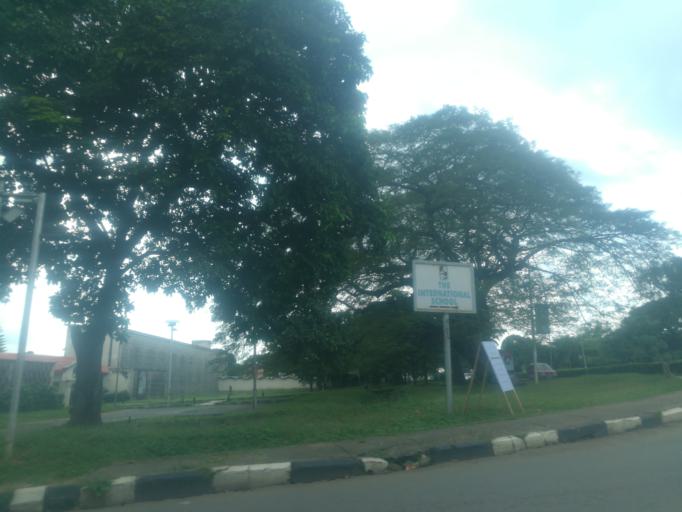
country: NG
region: Oyo
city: Ibadan
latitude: 7.4430
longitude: 3.9034
